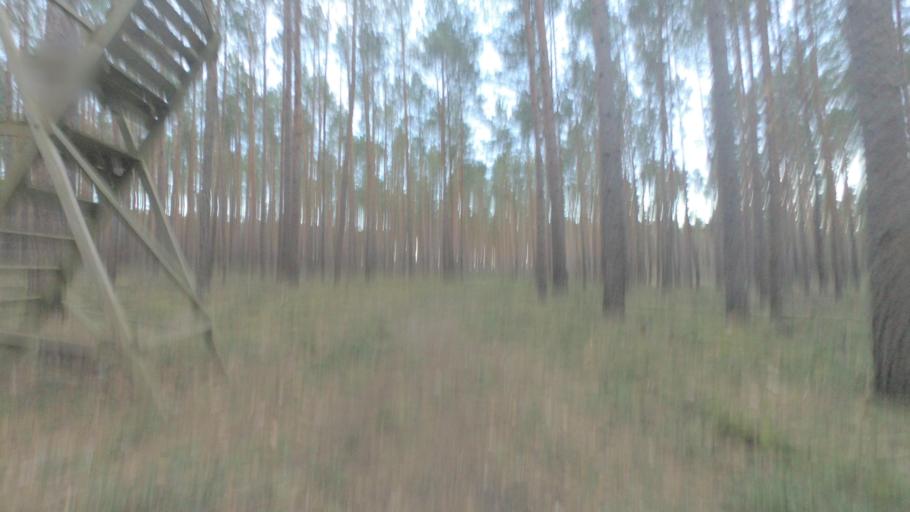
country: DE
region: Brandenburg
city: Rangsdorf
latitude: 52.2697
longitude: 13.3665
